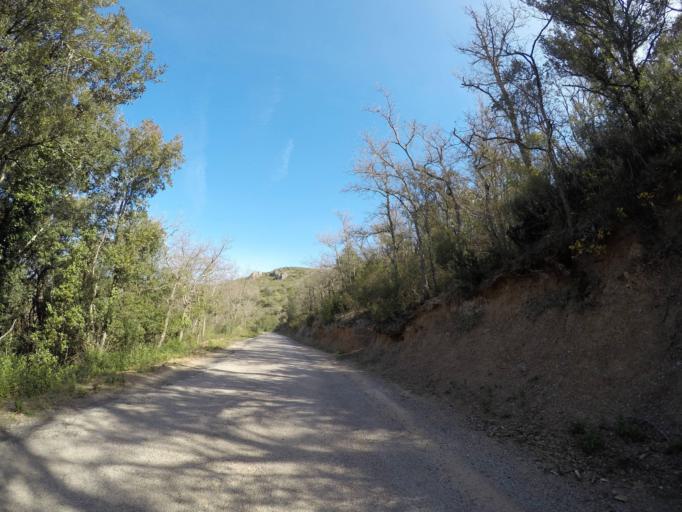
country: FR
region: Languedoc-Roussillon
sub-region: Departement des Pyrenees-Orientales
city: Thuir
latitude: 42.6271
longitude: 2.7046
